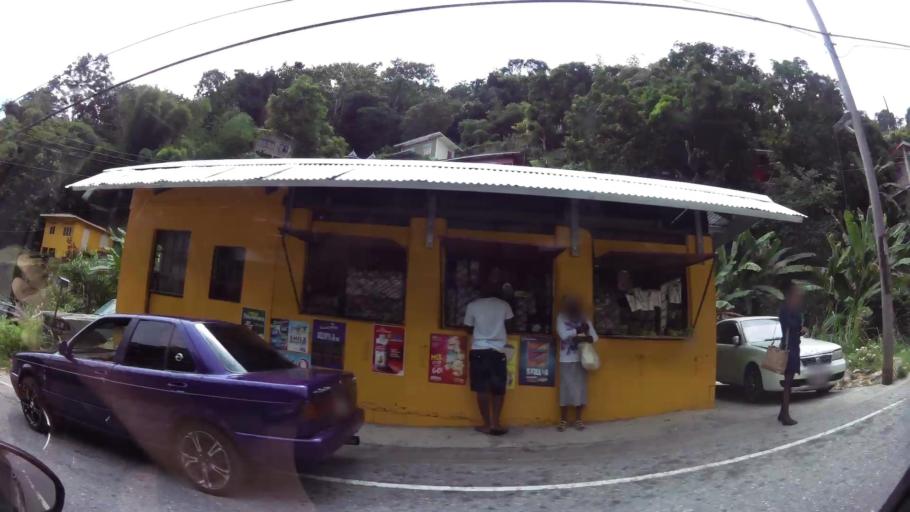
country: TT
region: Diego Martin
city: Petit Valley
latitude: 10.7149
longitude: -61.5195
